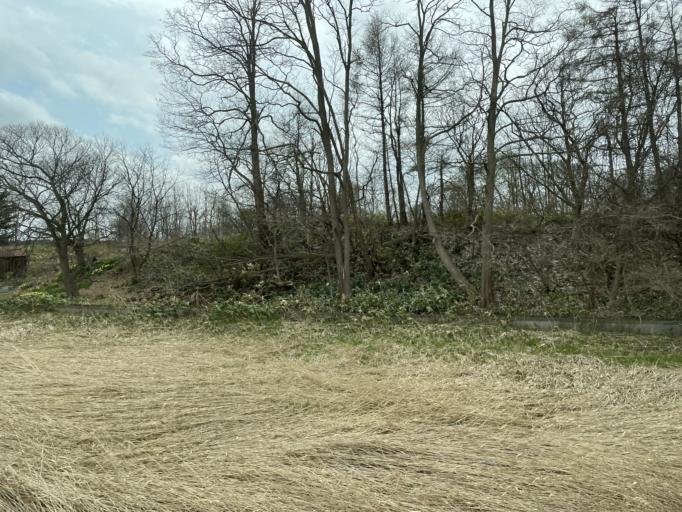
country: JP
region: Aomori
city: Shimokizukuri
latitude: 40.7861
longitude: 140.3094
